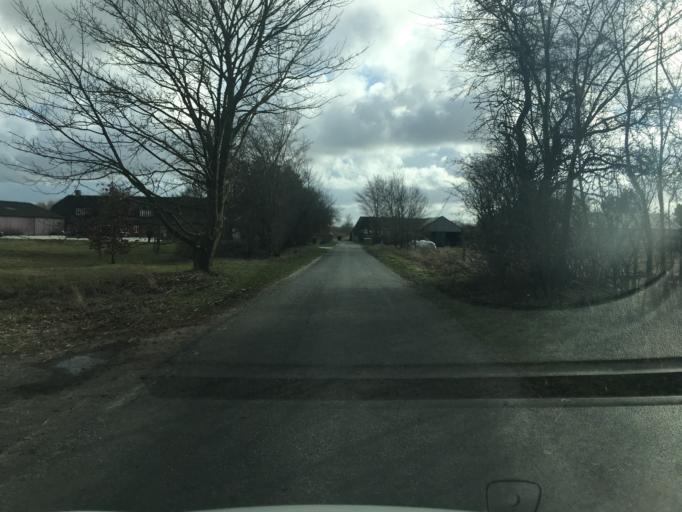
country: DK
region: South Denmark
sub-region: Aabenraa Kommune
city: Tinglev
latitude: 54.9212
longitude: 9.3377
